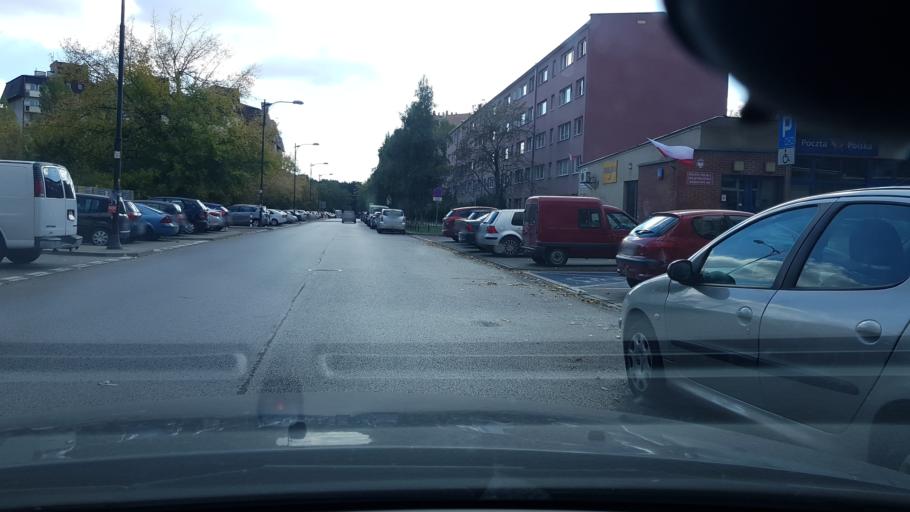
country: PL
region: Masovian Voivodeship
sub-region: Warszawa
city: Bielany
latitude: 52.2919
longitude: 20.9451
